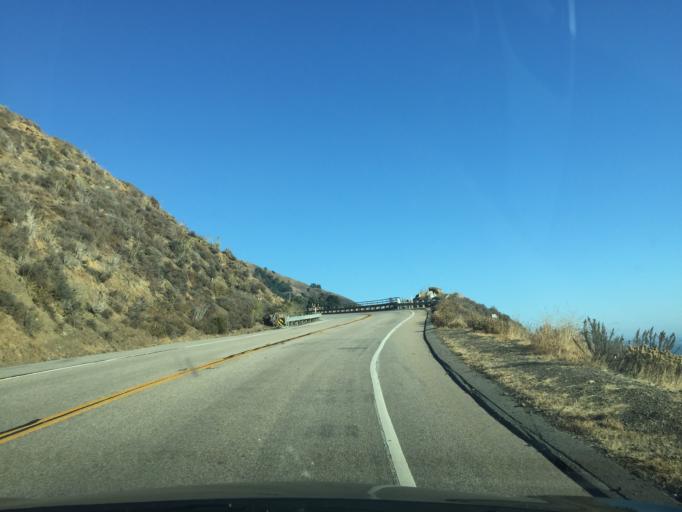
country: US
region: California
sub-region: San Luis Obispo County
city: Cambria
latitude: 35.8083
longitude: -121.3598
